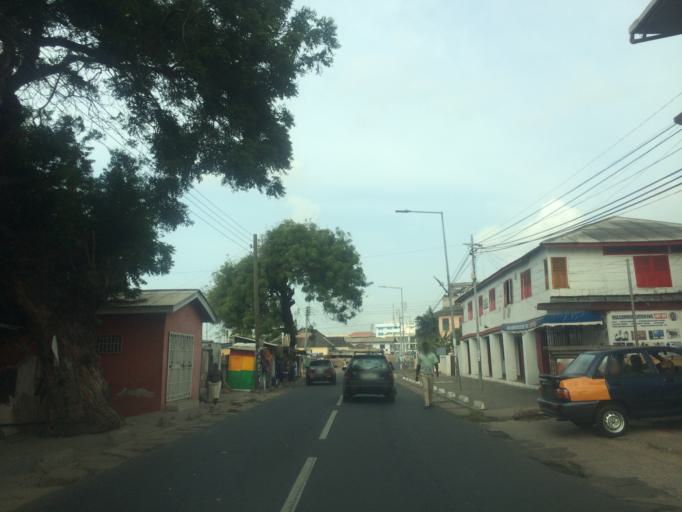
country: GH
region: Greater Accra
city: Accra
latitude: 5.5530
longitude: -0.1861
